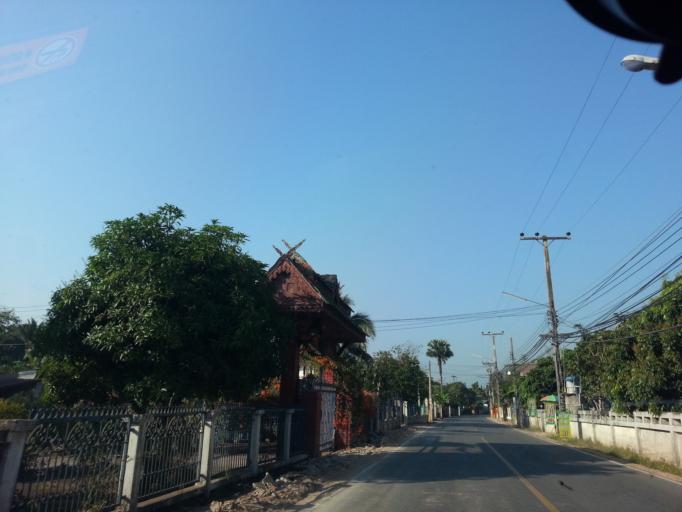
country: TH
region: Chiang Mai
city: San Sai
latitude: 18.8784
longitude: 99.0606
